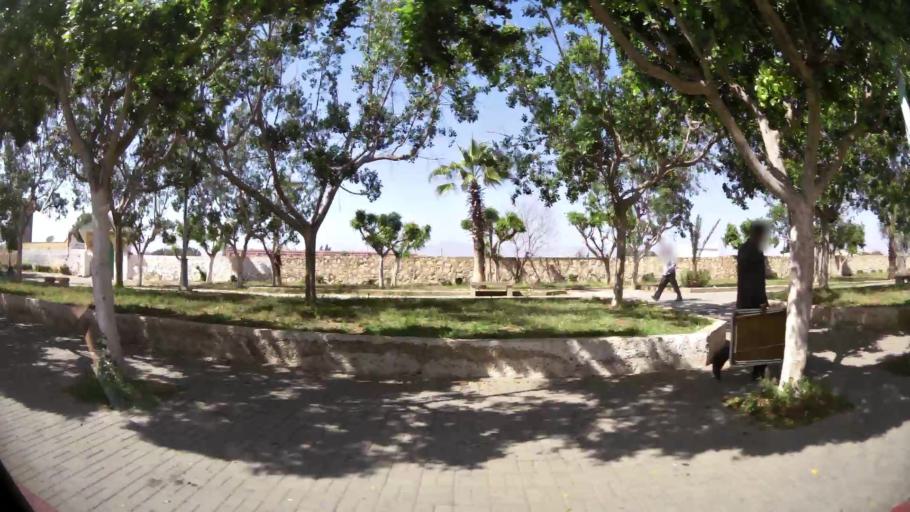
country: MA
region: Souss-Massa-Draa
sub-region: Inezgane-Ait Mellou
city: Inezgane
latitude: 30.3561
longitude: -9.5415
